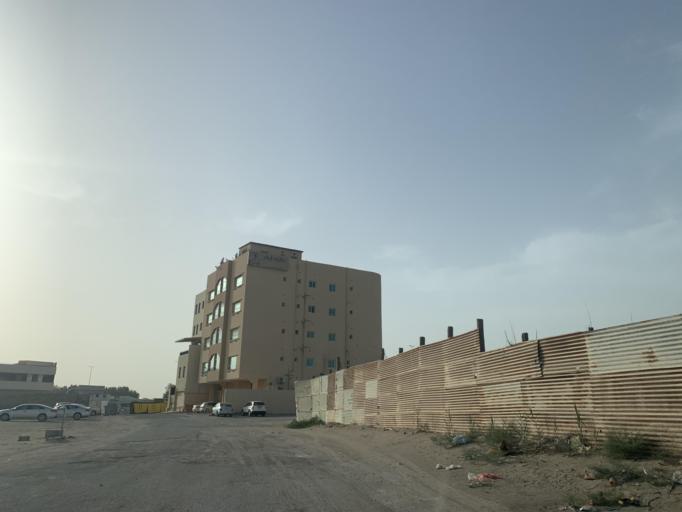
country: BH
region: Northern
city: Madinat `Isa
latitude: 26.1645
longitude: 50.5132
